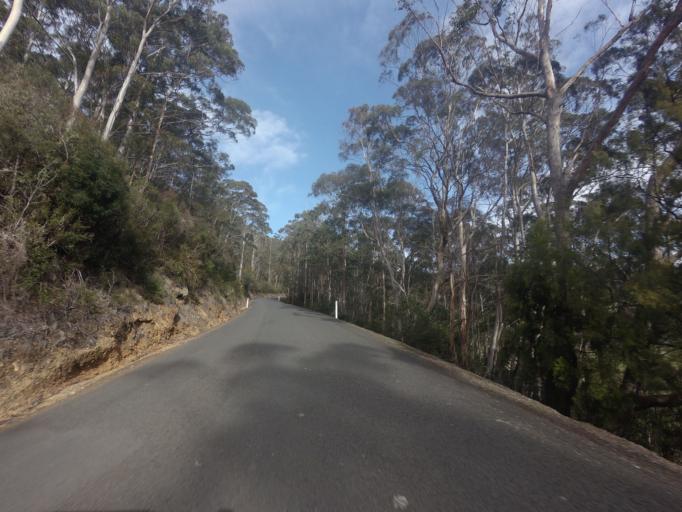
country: AU
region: Tasmania
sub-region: Kingborough
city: Margate
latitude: -43.0015
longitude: 147.1758
